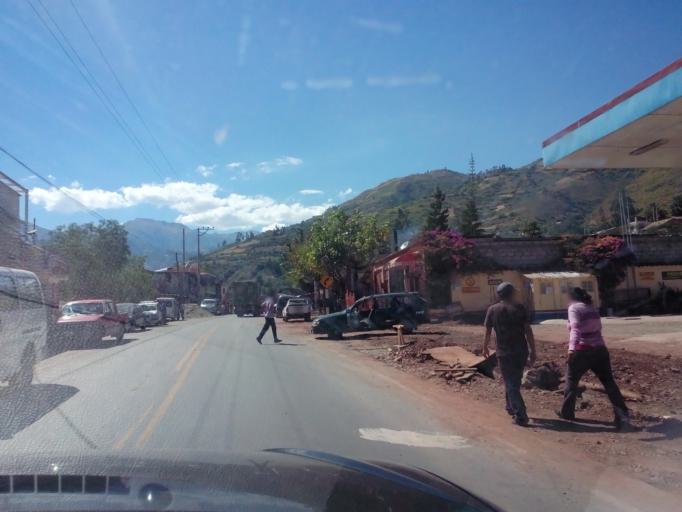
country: PE
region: Cusco
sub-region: Provincia de Anta
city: Limatambo
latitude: -13.4796
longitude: -72.4455
